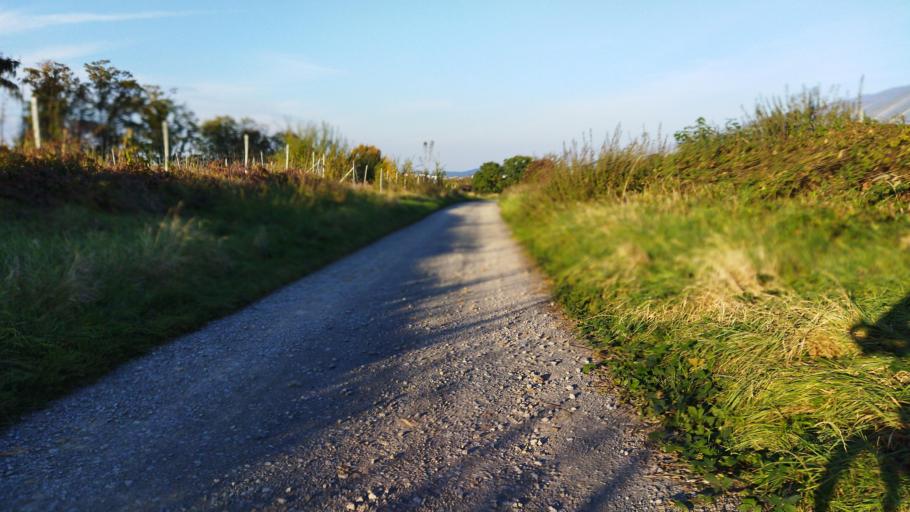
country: DE
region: Baden-Wuerttemberg
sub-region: Regierungsbezirk Stuttgart
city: Ilsfeld
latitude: 49.0359
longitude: 9.2676
